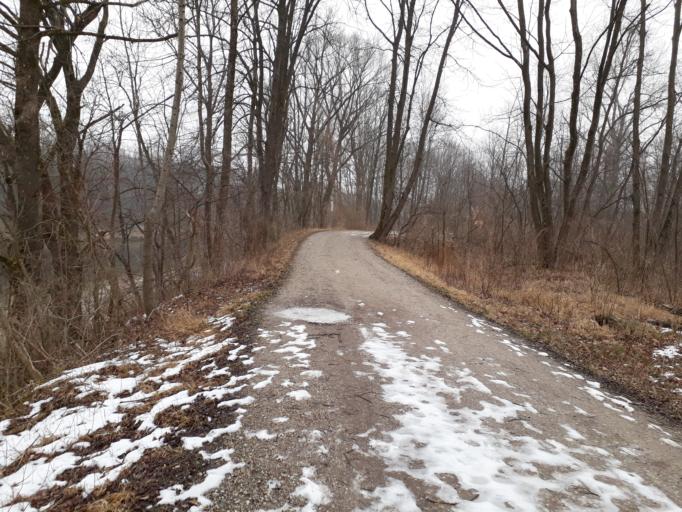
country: DE
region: Bavaria
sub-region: Upper Bavaria
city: Unterfoehring
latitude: 48.2197
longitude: 11.6527
